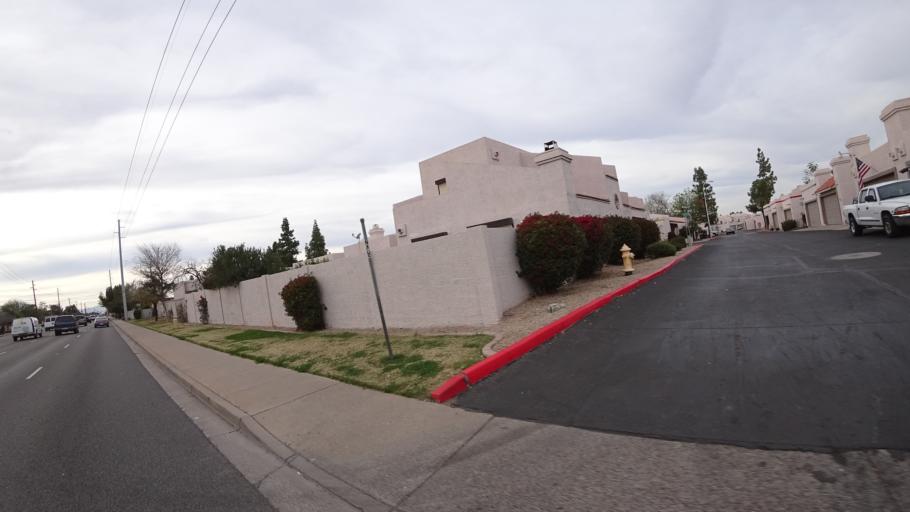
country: US
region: Arizona
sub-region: Maricopa County
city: Glendale
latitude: 33.5676
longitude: -112.1615
